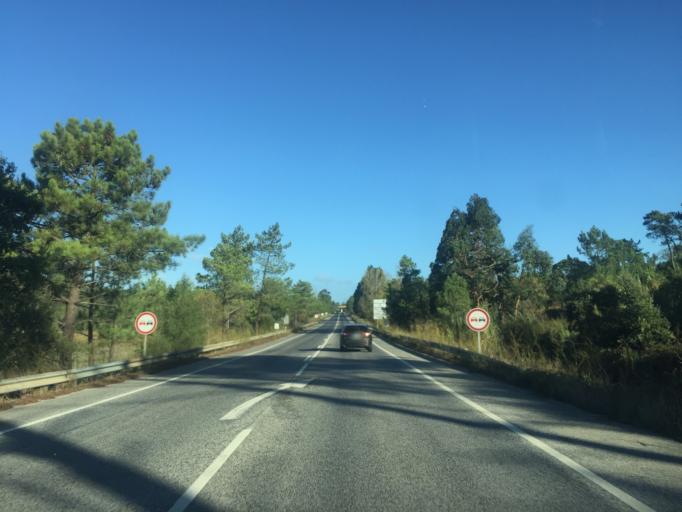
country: PT
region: Lisbon
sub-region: Azambuja
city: Alcoentre
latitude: 39.2197
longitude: -8.9542
